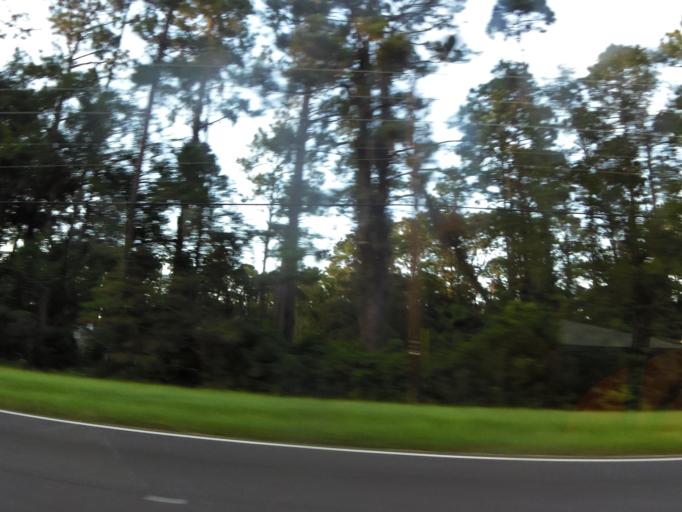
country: US
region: Georgia
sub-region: Camden County
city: Kingsland
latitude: 30.8011
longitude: -81.6815
